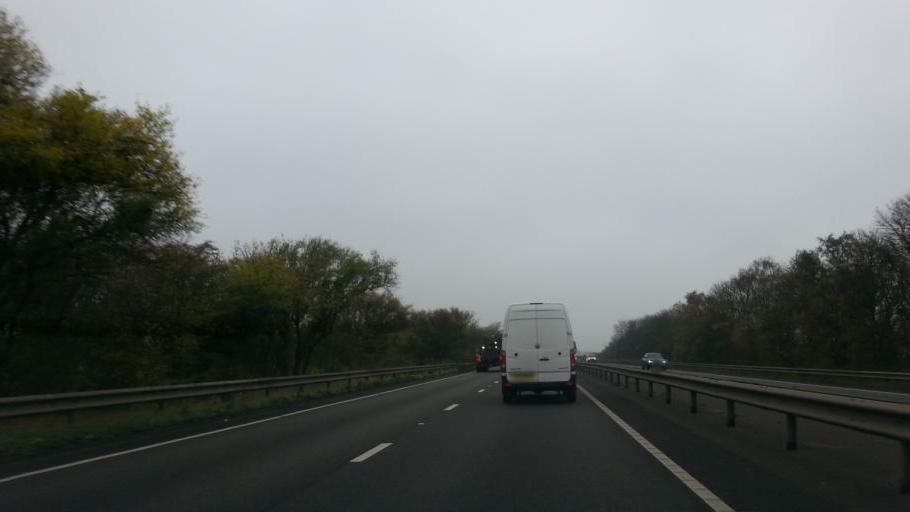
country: GB
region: England
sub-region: Nottinghamshire
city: South Collingham
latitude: 53.1774
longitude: -0.8170
